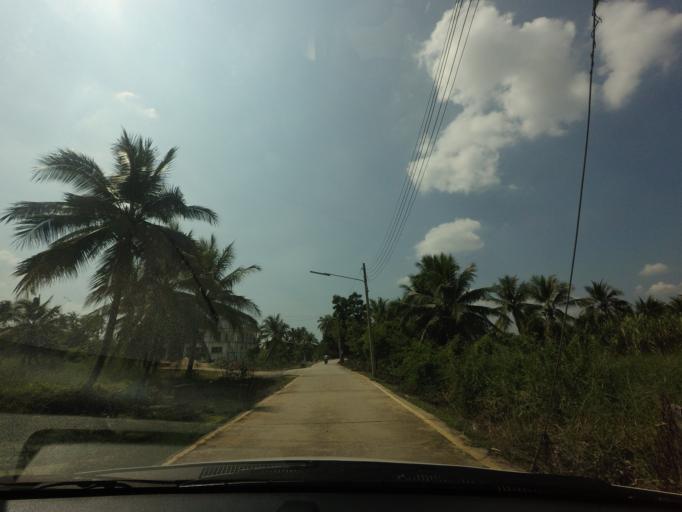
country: TH
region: Nakhon Pathom
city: Nakhon Chai Si
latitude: 13.8083
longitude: 100.1927
